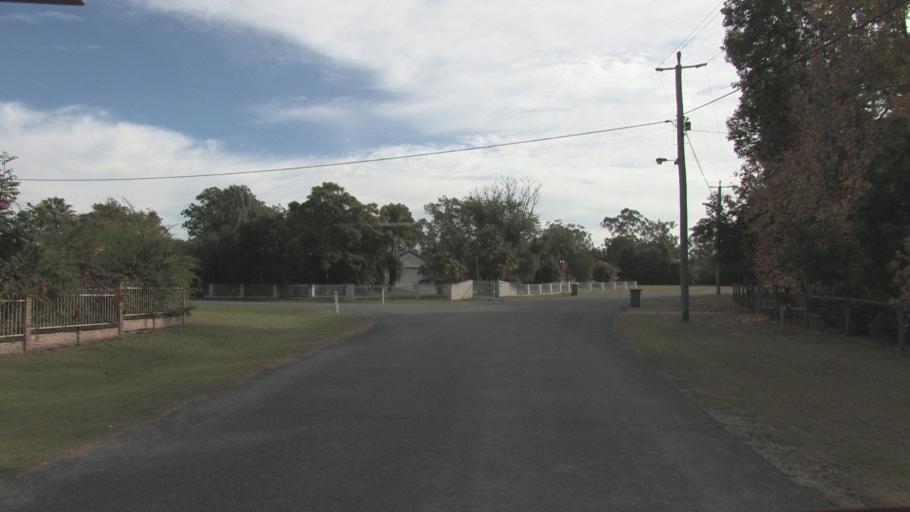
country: AU
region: Queensland
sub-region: Logan
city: Park Ridge South
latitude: -27.7399
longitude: 153.0433
